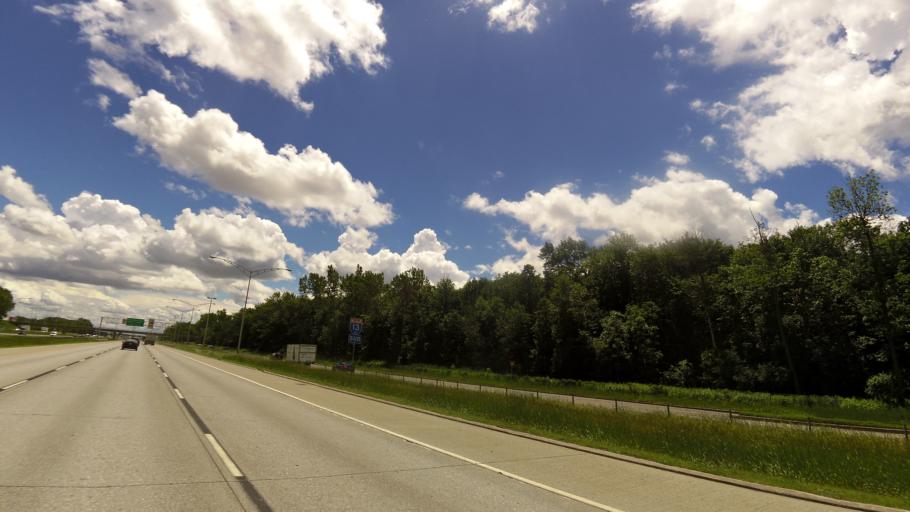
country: CA
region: Quebec
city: Dollard-Des Ormeaux
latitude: 45.5522
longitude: -73.8068
